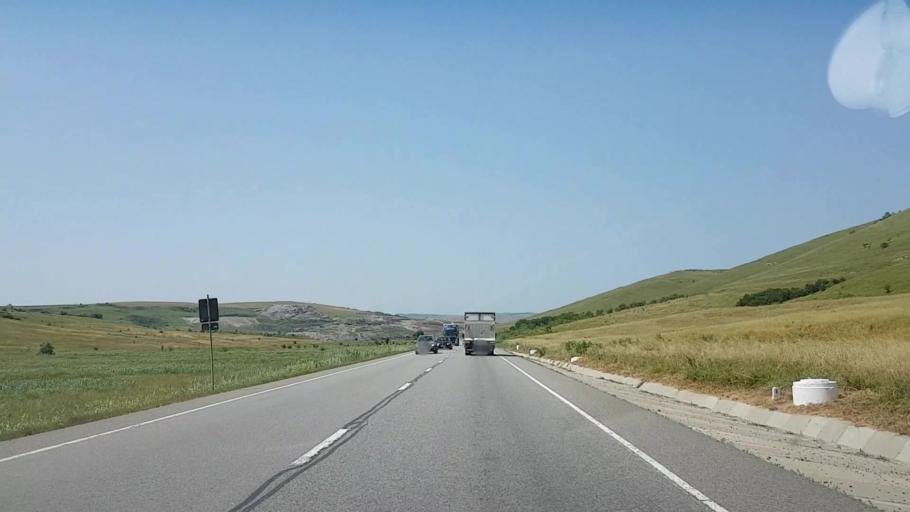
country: RO
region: Cluj
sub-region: Comuna Apahida
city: Dezmir
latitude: 46.7540
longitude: 23.7014
